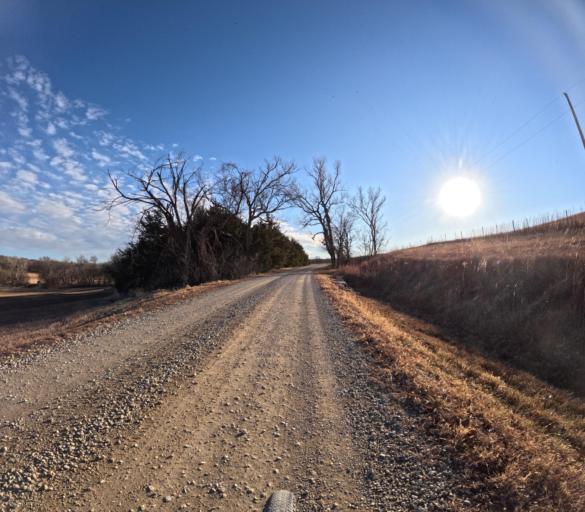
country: US
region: Kansas
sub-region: Riley County
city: Ogden
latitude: 39.2140
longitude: -96.6787
